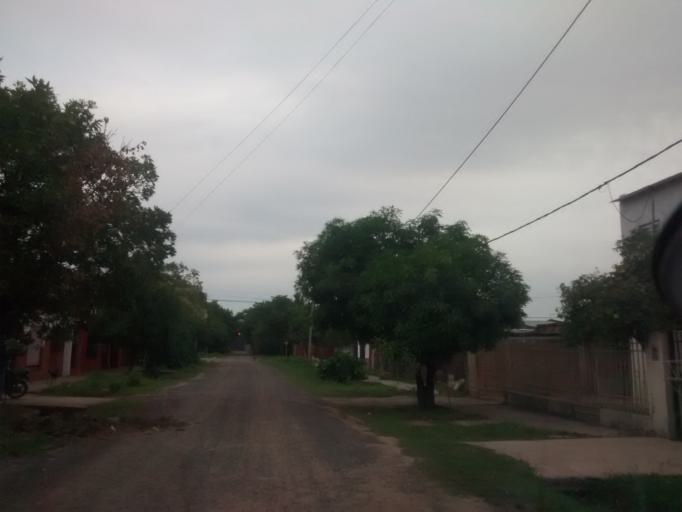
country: AR
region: Chaco
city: Resistencia
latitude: -27.4512
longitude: -59.0051
